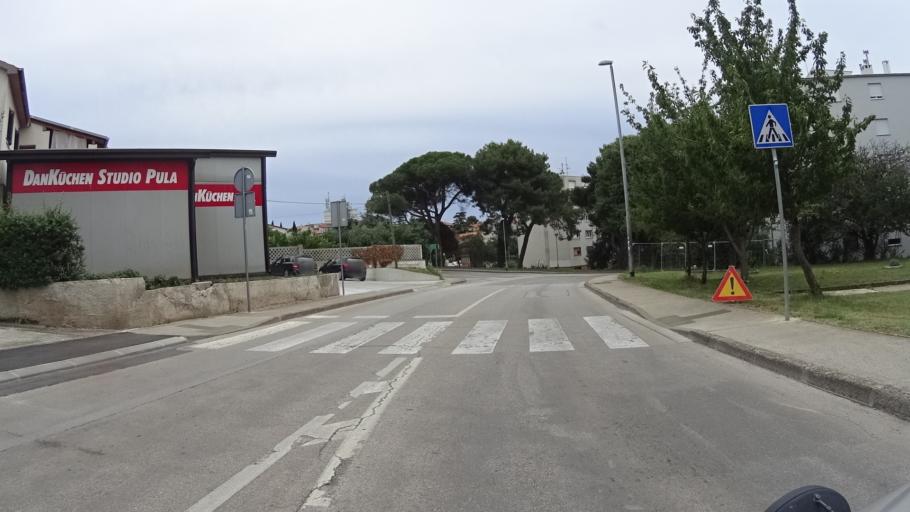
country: HR
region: Istarska
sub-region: Grad Pula
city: Pula
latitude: 44.8570
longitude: 13.8440
